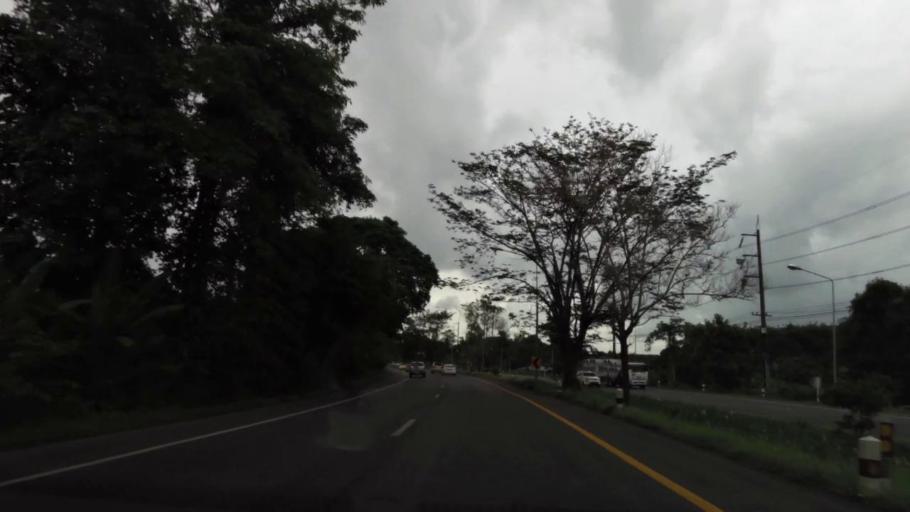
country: TH
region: Chanthaburi
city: Tha Mai
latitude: 12.6825
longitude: 102.0049
